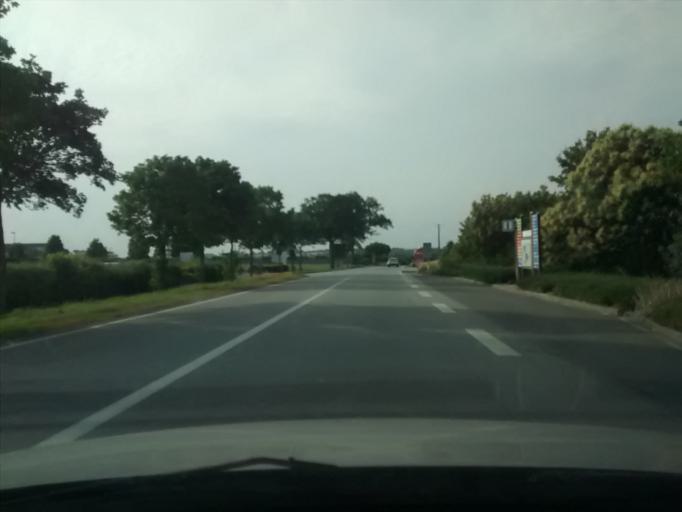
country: FR
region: Brittany
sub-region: Departement d'Ille-et-Vilaine
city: Etrelles
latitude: 48.0731
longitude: -1.1997
